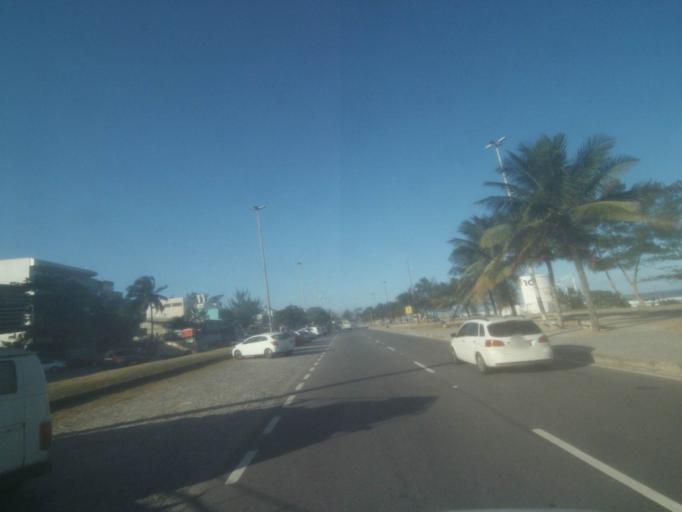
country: BR
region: Rio de Janeiro
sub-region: Nilopolis
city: Nilopolis
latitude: -23.0256
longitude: -43.4590
